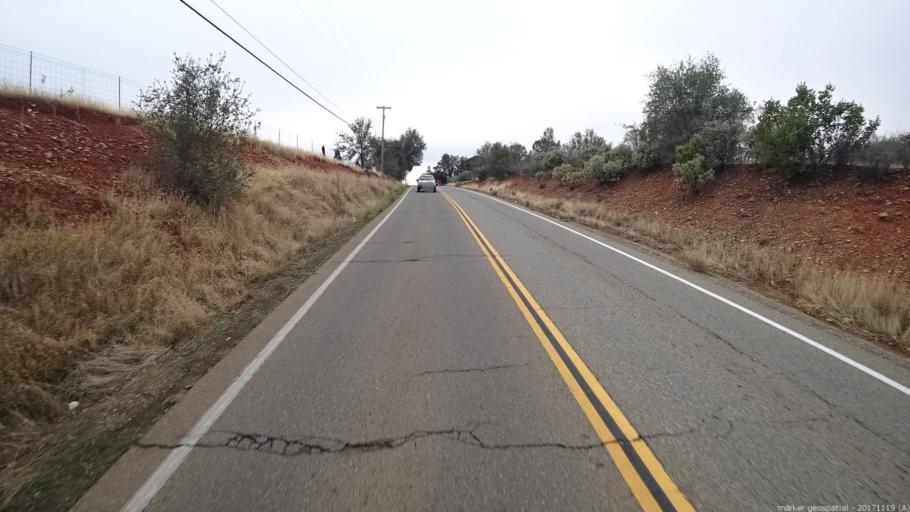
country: US
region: California
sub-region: Shasta County
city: Anderson
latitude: 40.4810
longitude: -122.3976
